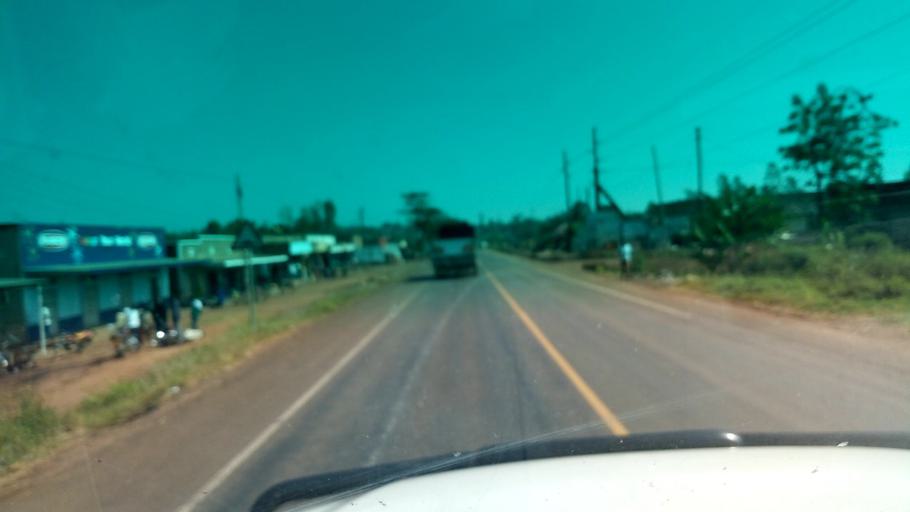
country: UG
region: Western Region
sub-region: Kiryandongo District
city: Kiryandongo
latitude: 1.9407
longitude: 32.1301
